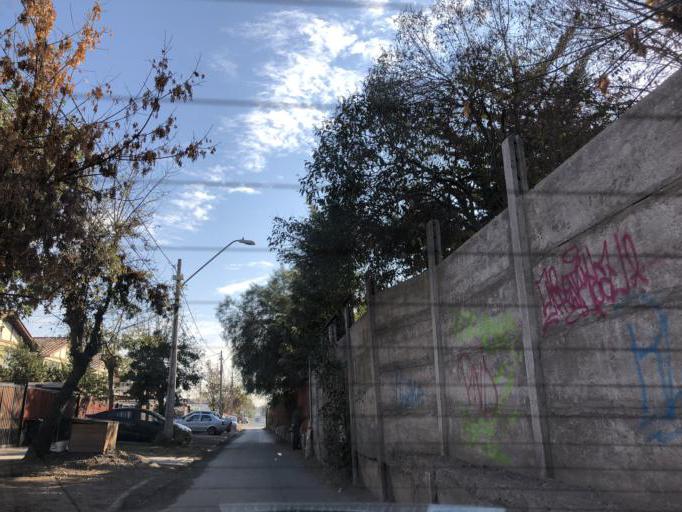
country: CL
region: Santiago Metropolitan
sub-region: Provincia de Cordillera
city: Puente Alto
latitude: -33.6325
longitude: -70.5925
